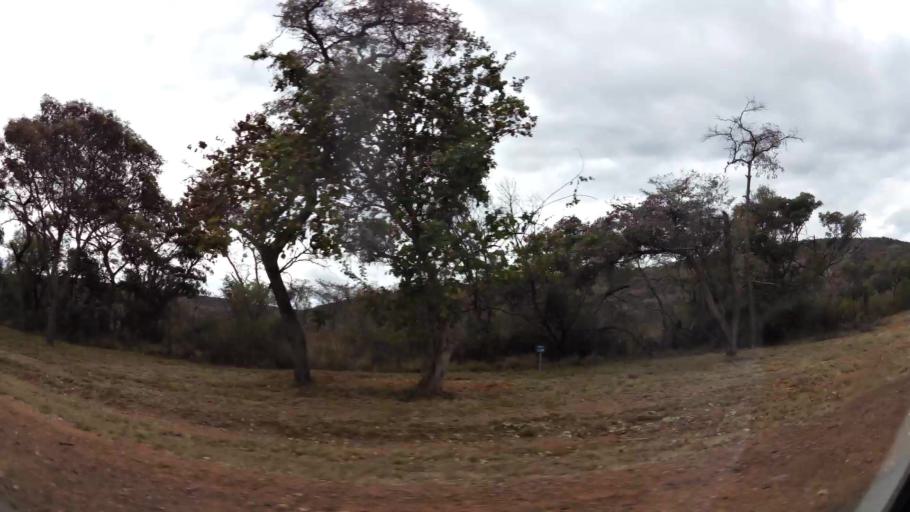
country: ZA
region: Limpopo
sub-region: Waterberg District Municipality
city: Modimolle
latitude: -24.6786
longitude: 28.5280
